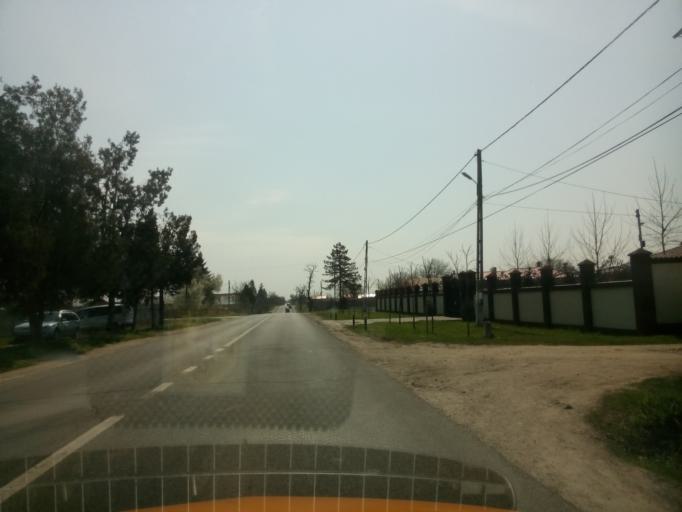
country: RO
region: Calarasi
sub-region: Comuna Frumusani
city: Frumusani
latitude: 44.2999
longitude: 26.3082
